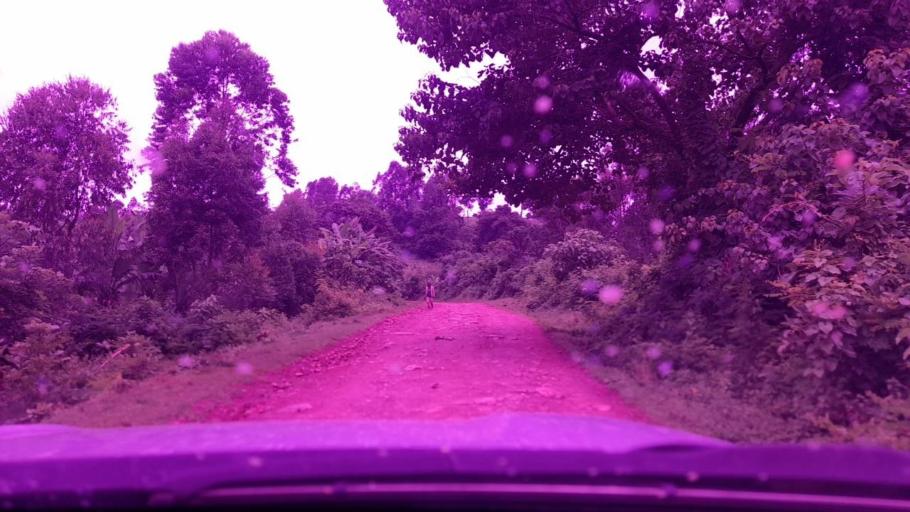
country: ET
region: Southern Nations, Nationalities, and People's Region
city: Bonga
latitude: 7.5497
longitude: 35.8505
